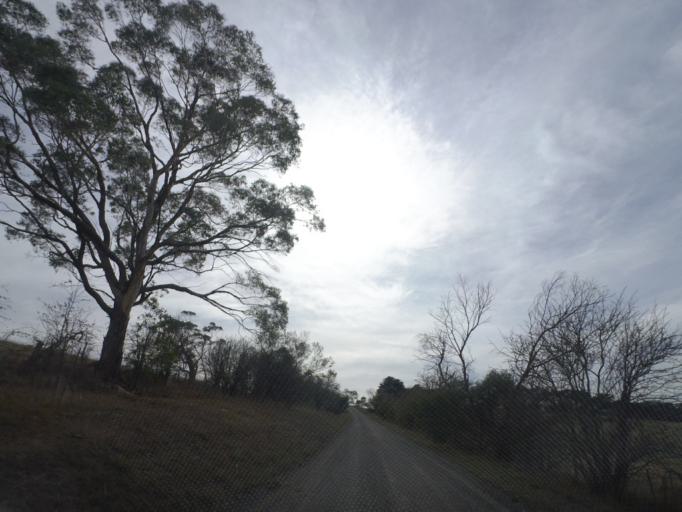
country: AU
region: Victoria
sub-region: Yarra Ranges
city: Yarra Glen
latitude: -37.6413
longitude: 145.4234
